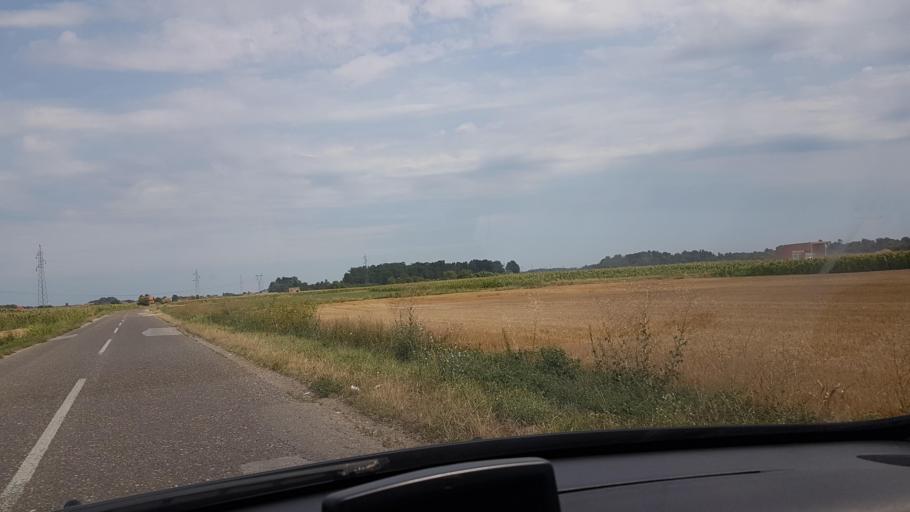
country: BA
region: Republika Srpska
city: Bijeljina
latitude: 44.7910
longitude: 19.2216
